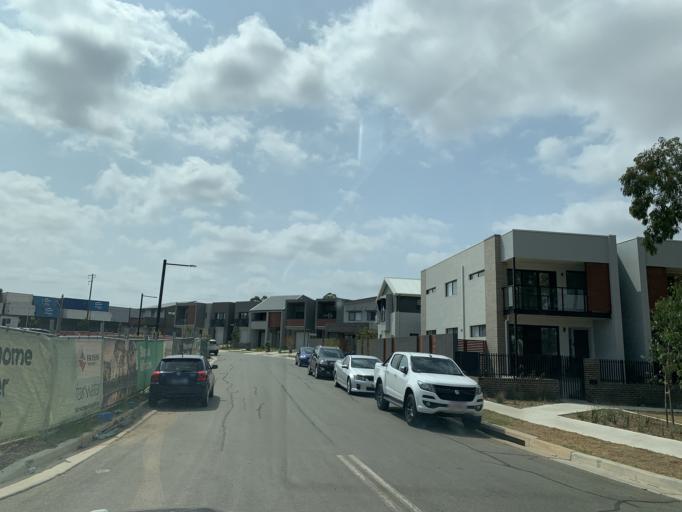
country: AU
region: New South Wales
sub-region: Blacktown
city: Blacktown
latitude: -33.7557
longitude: 150.9022
